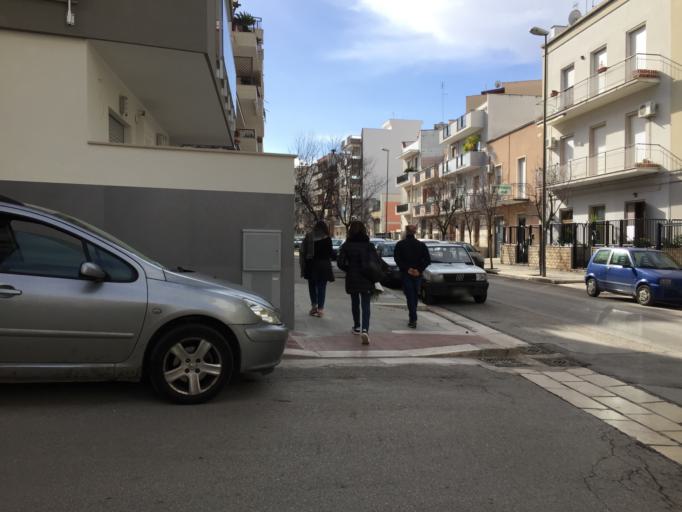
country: IT
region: Apulia
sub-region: Provincia di Barletta - Andria - Trani
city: Andria
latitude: 41.2197
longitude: 16.2996
